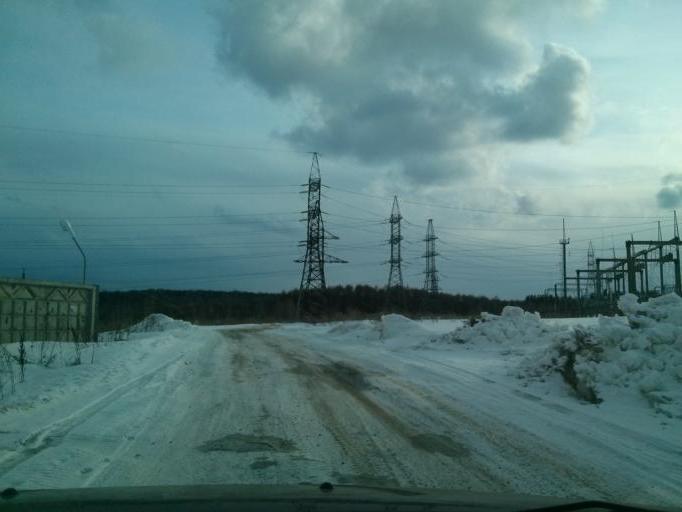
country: RU
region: Nizjnij Novgorod
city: Afonino
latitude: 56.2641
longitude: 44.0310
